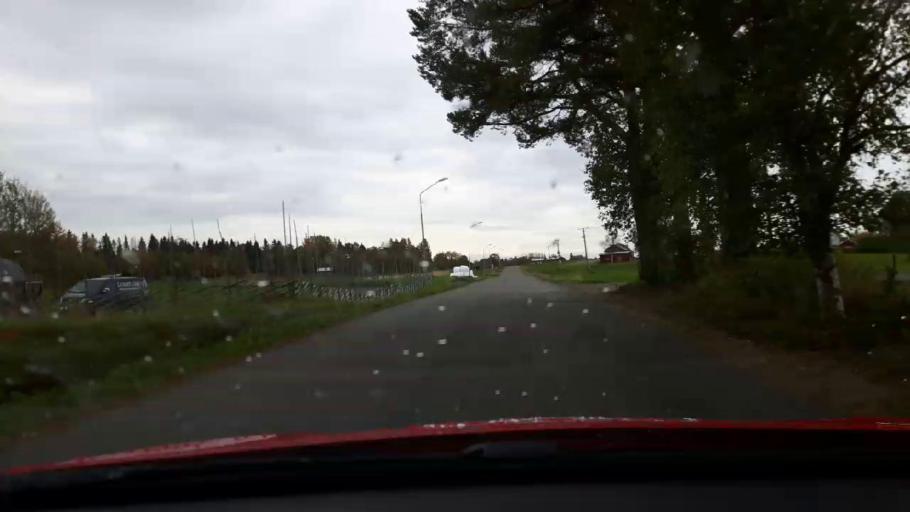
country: SE
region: Jaemtland
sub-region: Bergs Kommun
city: Hoverberg
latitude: 62.9465
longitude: 14.4933
